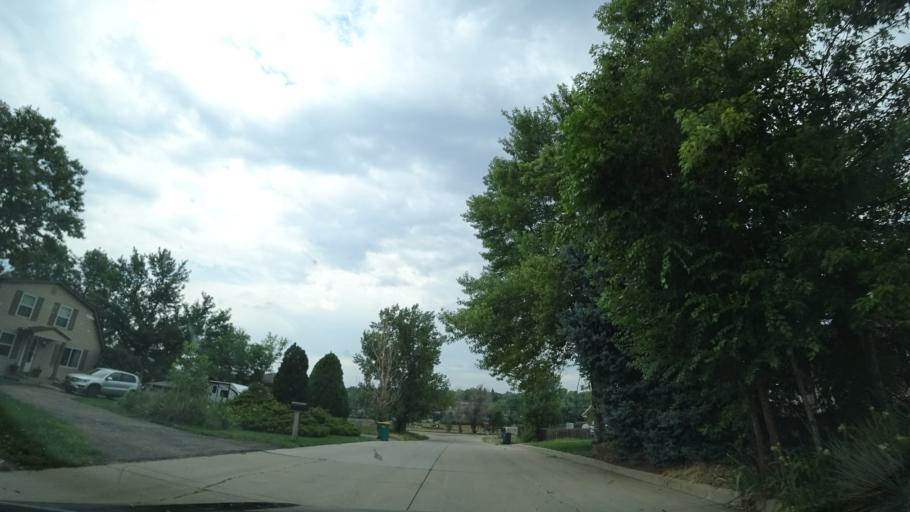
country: US
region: Colorado
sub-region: Jefferson County
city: Lakewood
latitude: 39.7029
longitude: -105.0688
